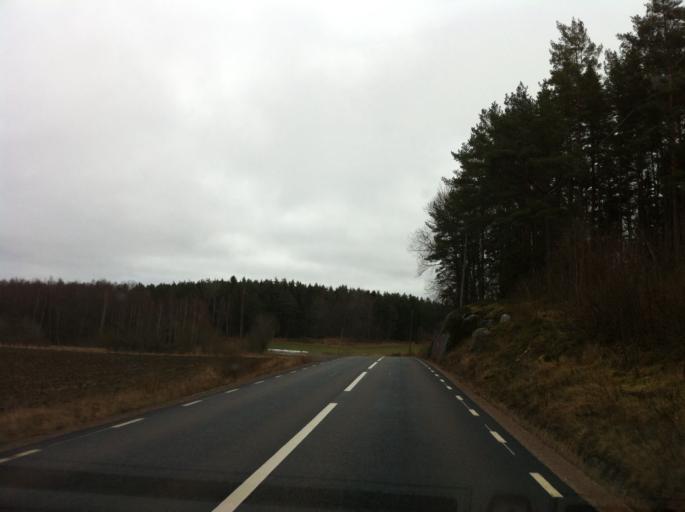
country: SE
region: Kalmar
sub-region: Vasterviks Kommun
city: Overum
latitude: 57.9051
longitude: 16.2090
